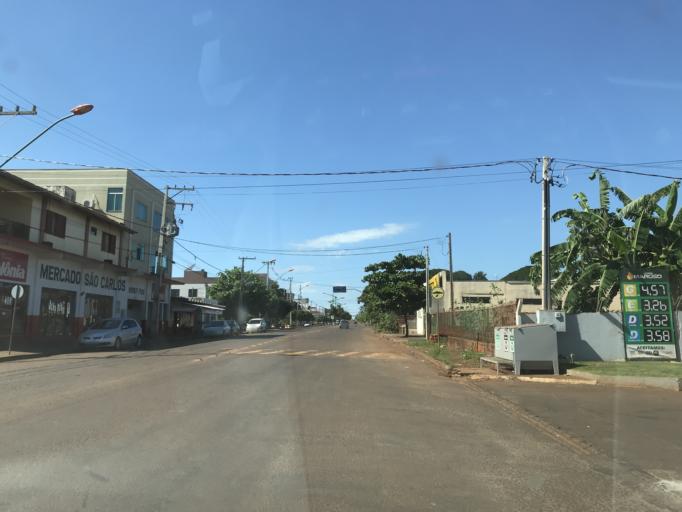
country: BR
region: Parana
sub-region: Palotina
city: Palotina
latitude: -24.2855
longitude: -53.8481
